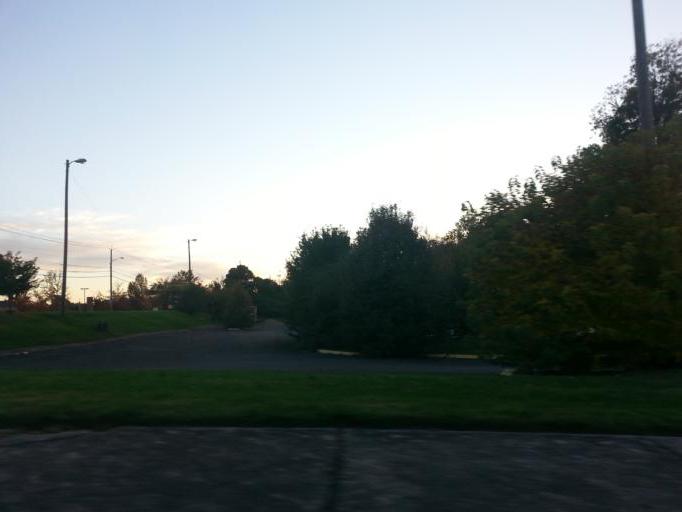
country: US
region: Tennessee
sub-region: Knox County
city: Knoxville
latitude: 35.9576
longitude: -83.9518
